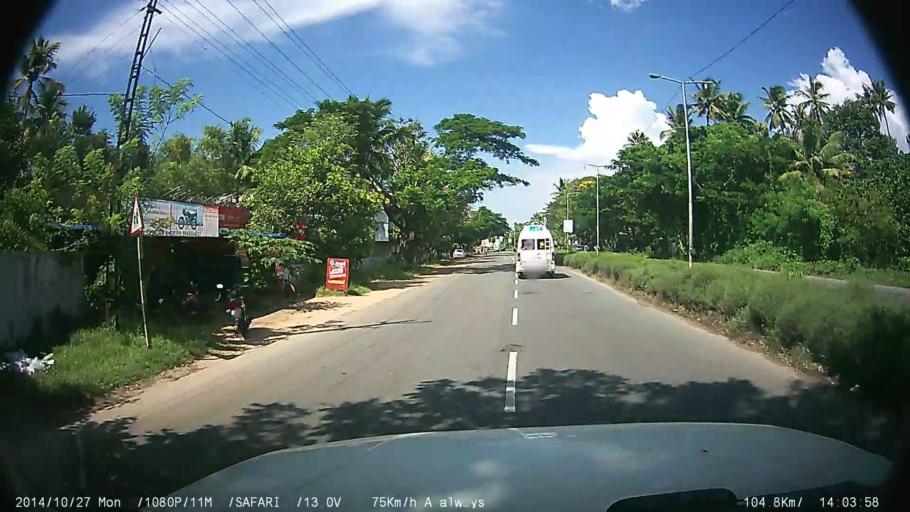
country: IN
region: Kerala
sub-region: Alappuzha
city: Vayalar
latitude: 9.7272
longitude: 76.3187
